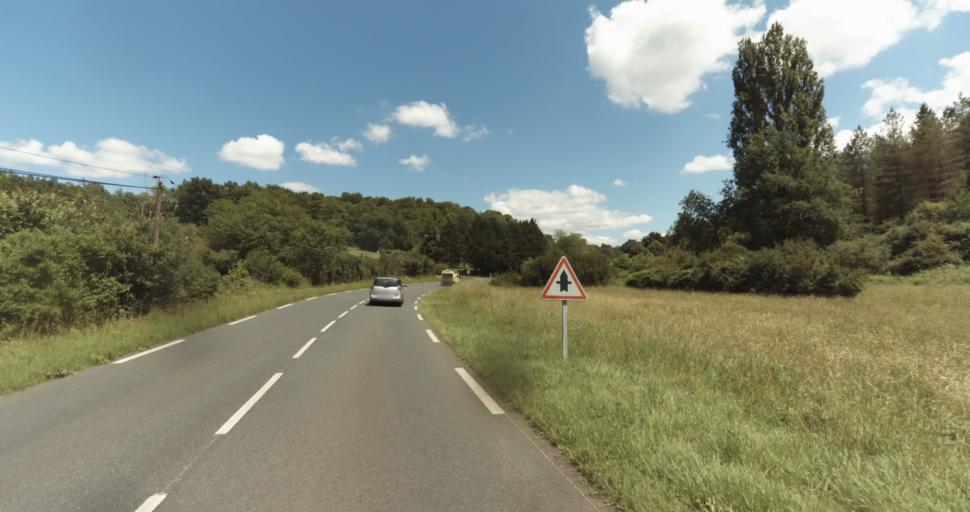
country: FR
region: Aquitaine
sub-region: Departement de la Dordogne
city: Le Bugue
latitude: 44.8410
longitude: 0.8561
